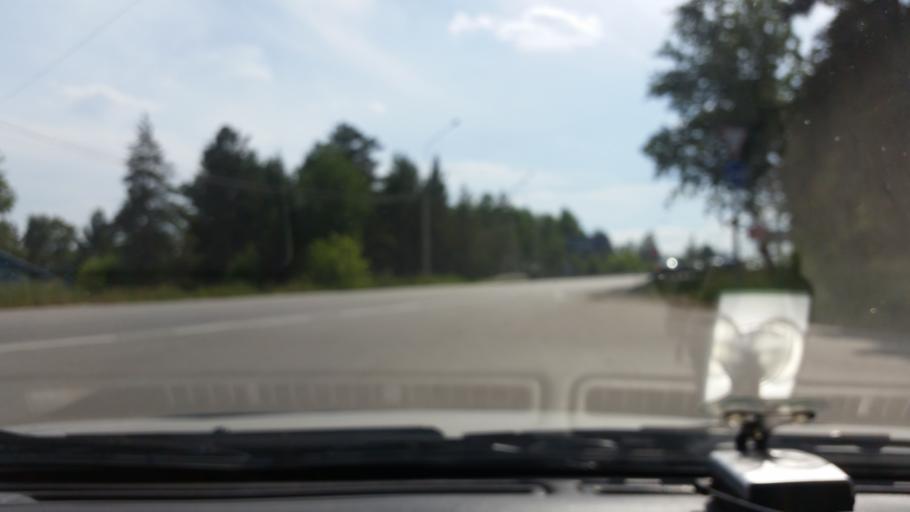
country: RU
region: Irkutsk
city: Shelekhov
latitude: 52.2120
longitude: 104.1117
